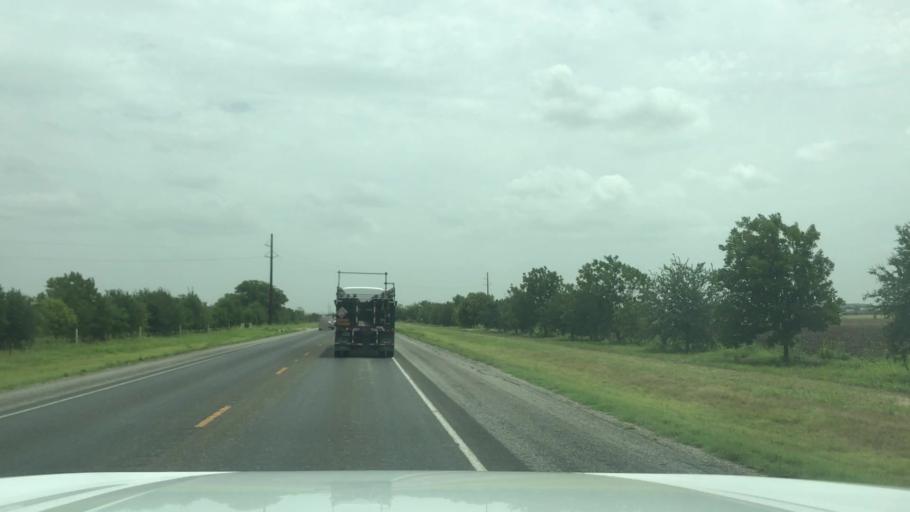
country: US
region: Texas
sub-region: Bosque County
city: Clifton
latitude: 31.7996
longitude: -97.5966
